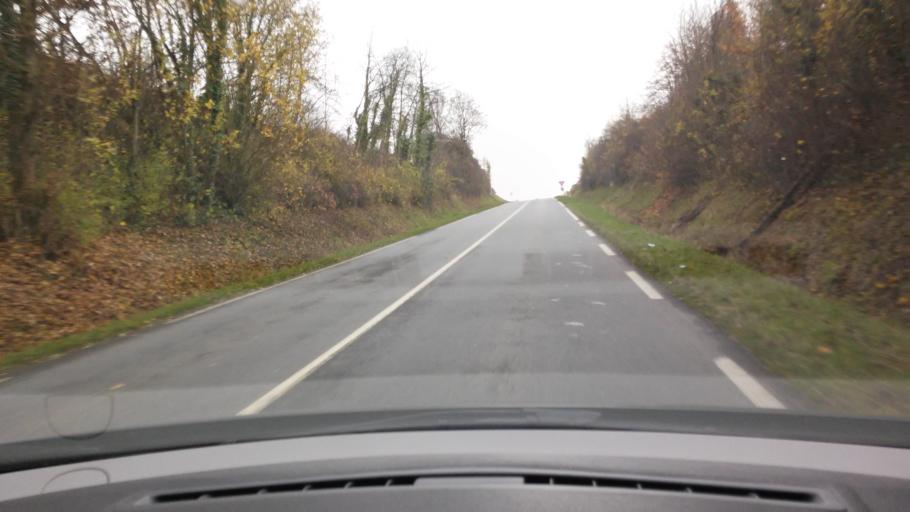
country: FR
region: Lorraine
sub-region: Departement de la Moselle
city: Saint-Julien-les-Metz
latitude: 49.1505
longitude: 6.2481
